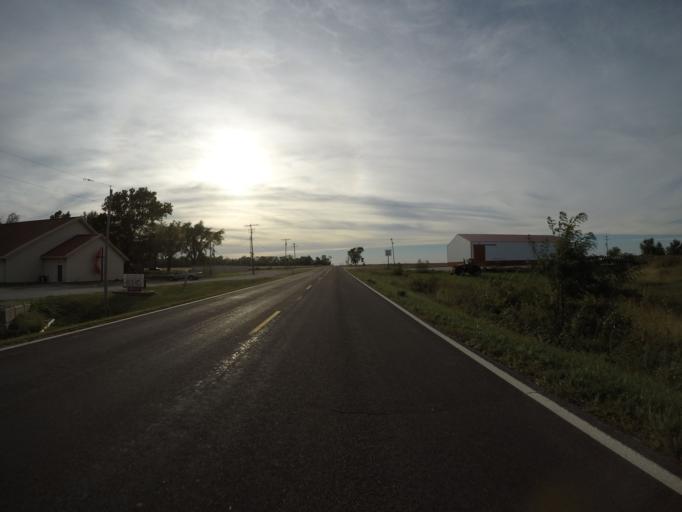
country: US
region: Kansas
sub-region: Douglas County
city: Baldwin City
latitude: 38.7824
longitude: -95.3336
